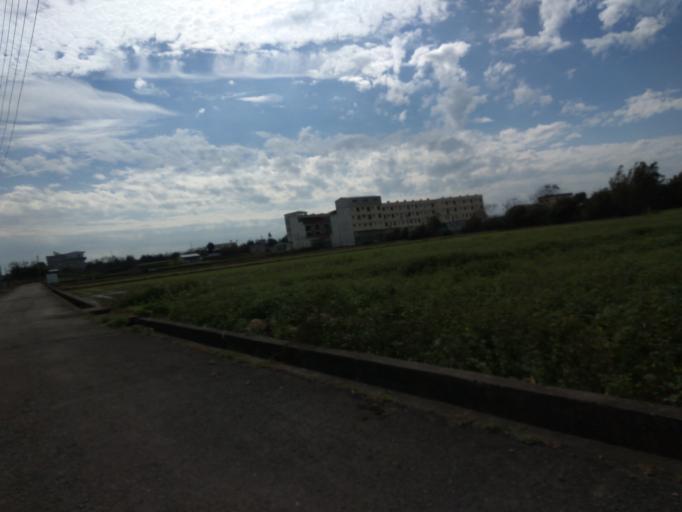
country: TW
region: Taiwan
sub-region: Hsinchu
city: Zhubei
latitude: 24.9859
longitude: 121.0892
